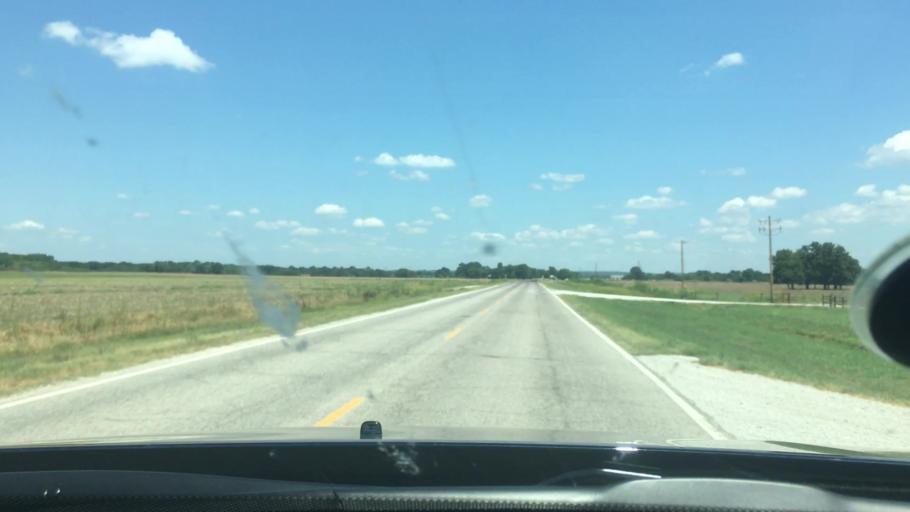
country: US
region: Oklahoma
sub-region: Carter County
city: Dickson
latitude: 34.2218
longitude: -96.9771
